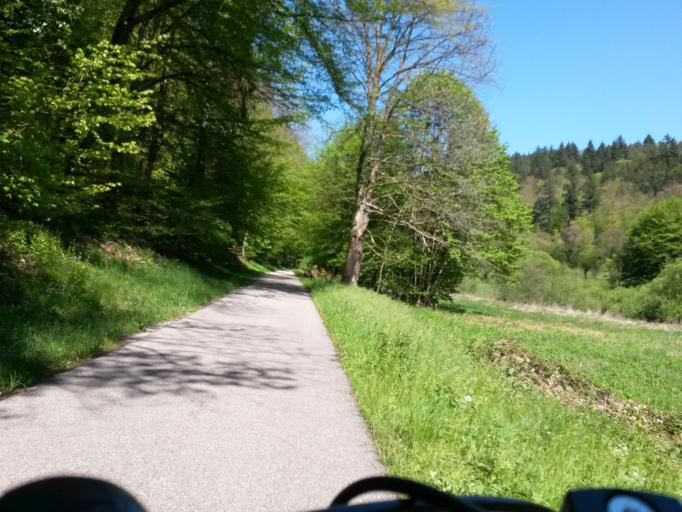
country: DE
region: Baden-Wuerttemberg
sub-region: Karlsruhe Region
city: Unterreichenbach
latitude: 48.8512
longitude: 8.6858
